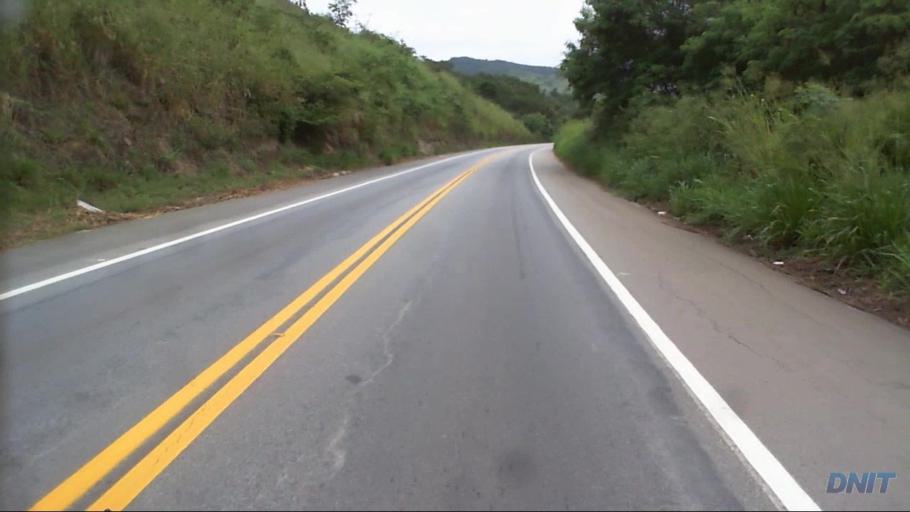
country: BR
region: Minas Gerais
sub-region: Timoteo
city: Timoteo
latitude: -19.5902
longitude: -42.7358
